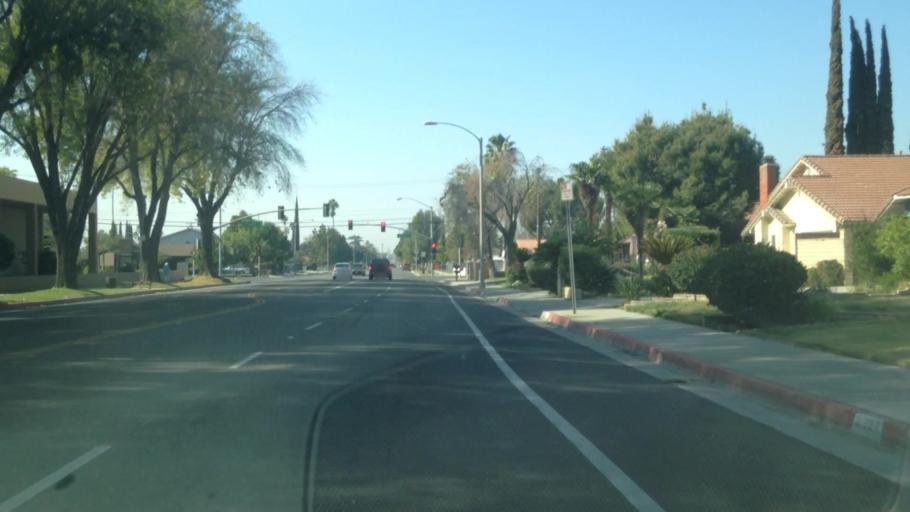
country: US
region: California
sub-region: Riverside County
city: Riverside
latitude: 33.9534
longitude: -117.4175
